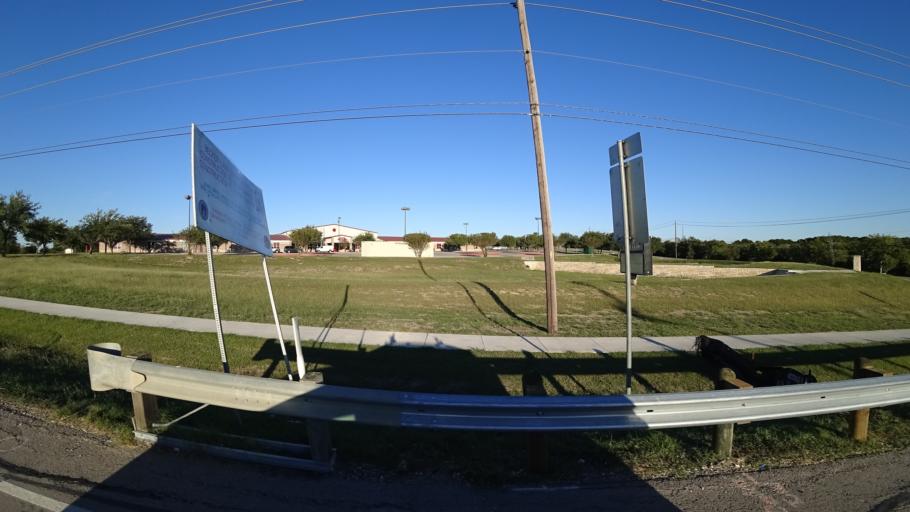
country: US
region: Texas
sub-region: Travis County
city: Manor
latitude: 30.3112
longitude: -97.6151
